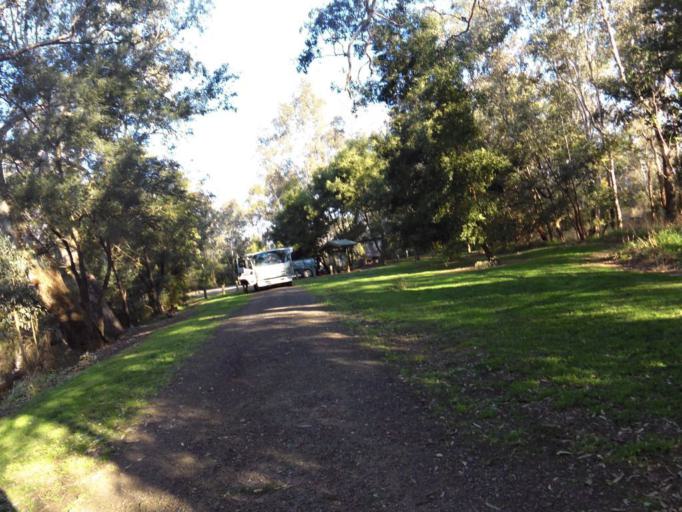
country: AU
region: Victoria
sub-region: Murrindindi
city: Alexandra
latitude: -37.2078
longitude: 145.4298
